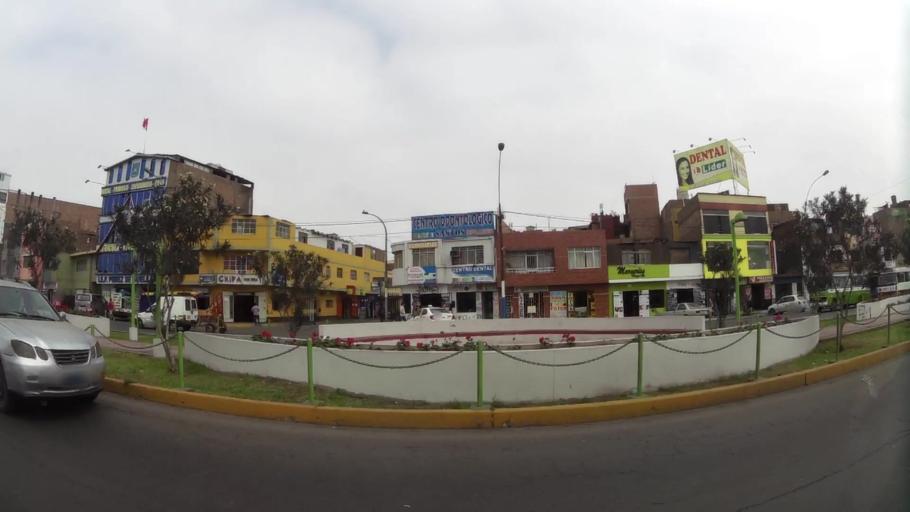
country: PE
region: Callao
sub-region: Callao
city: Callao
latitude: -12.0306
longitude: -77.0877
